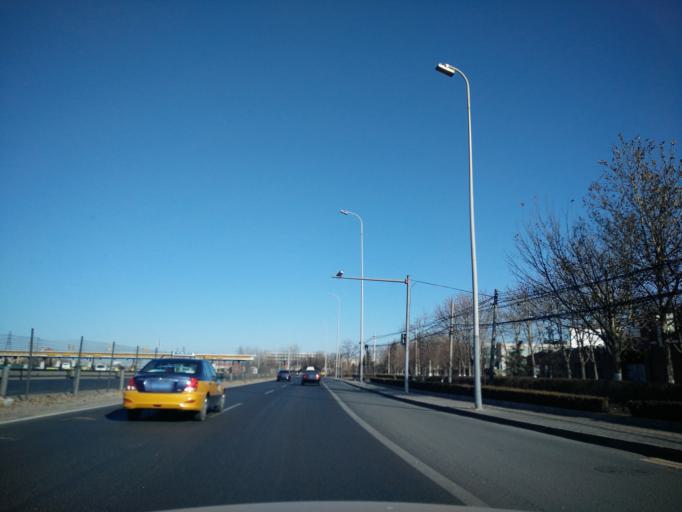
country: CN
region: Beijing
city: Xihongmen
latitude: 39.7943
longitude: 116.3420
